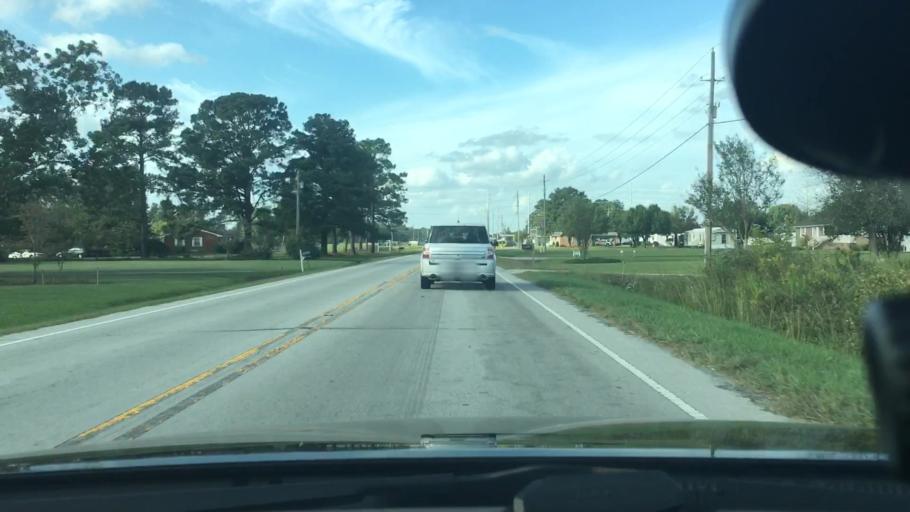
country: US
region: North Carolina
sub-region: Pitt County
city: Windsor
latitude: 35.5276
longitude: -77.3195
